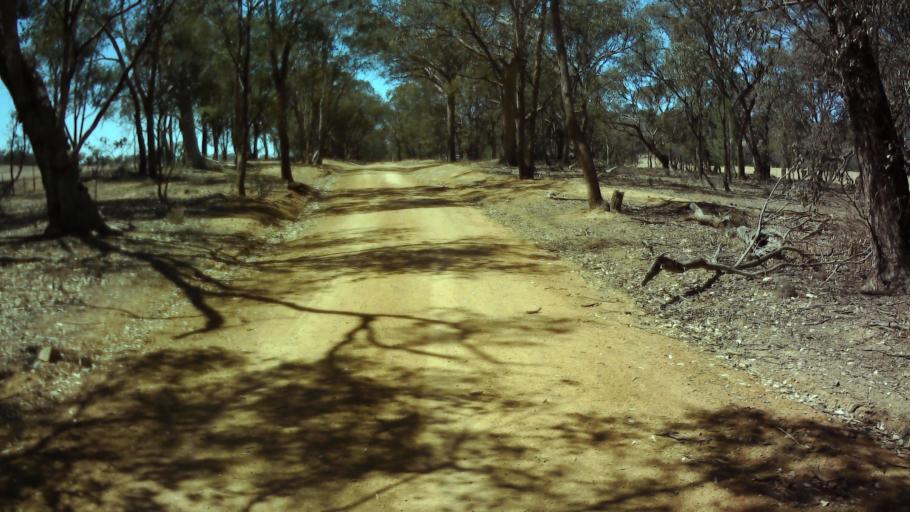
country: AU
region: New South Wales
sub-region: Weddin
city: Grenfell
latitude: -33.9570
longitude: 148.0849
